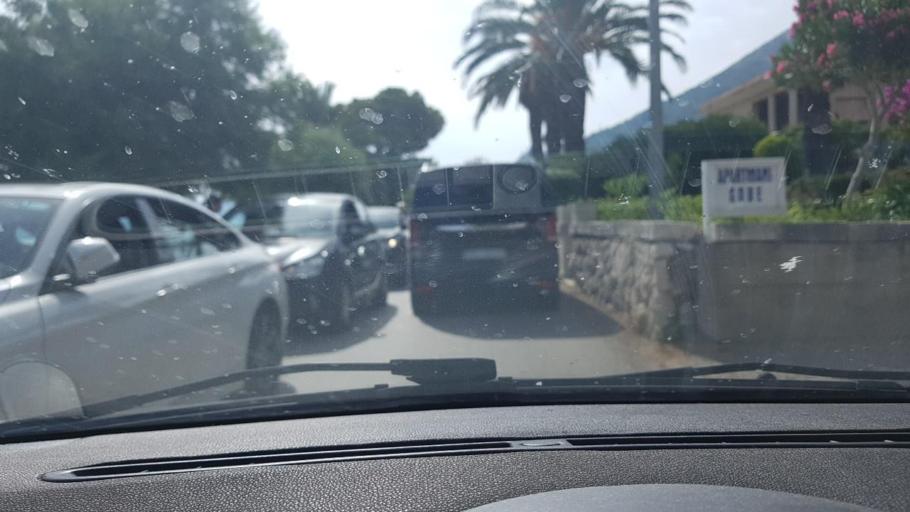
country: HR
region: Dubrovacko-Neretvanska
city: Orebic
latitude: 42.9749
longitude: 17.1738
